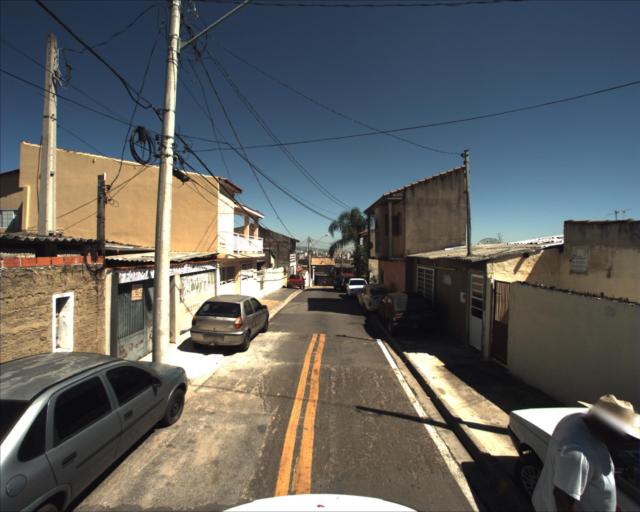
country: BR
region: Sao Paulo
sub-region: Votorantim
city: Votorantim
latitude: -23.5227
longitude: -47.4314
